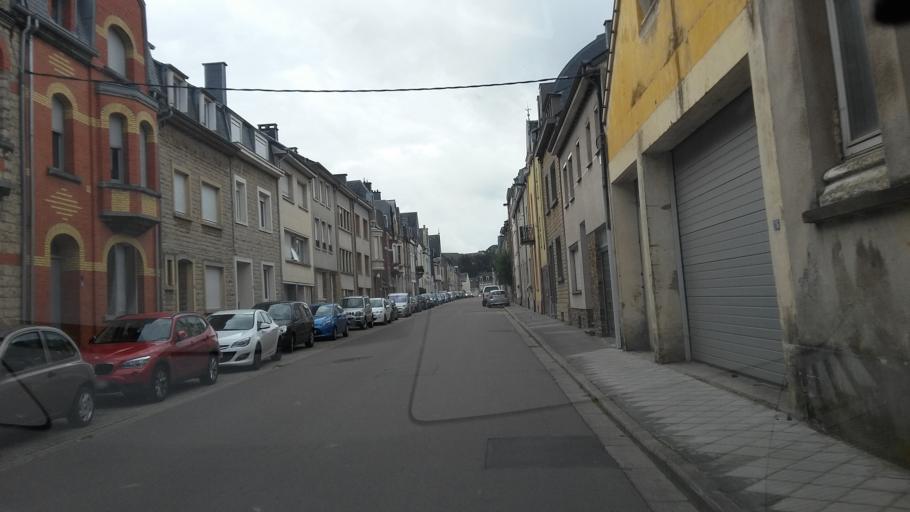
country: BE
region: Wallonia
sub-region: Province du Luxembourg
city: Arlon
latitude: 49.6886
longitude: 5.8067
